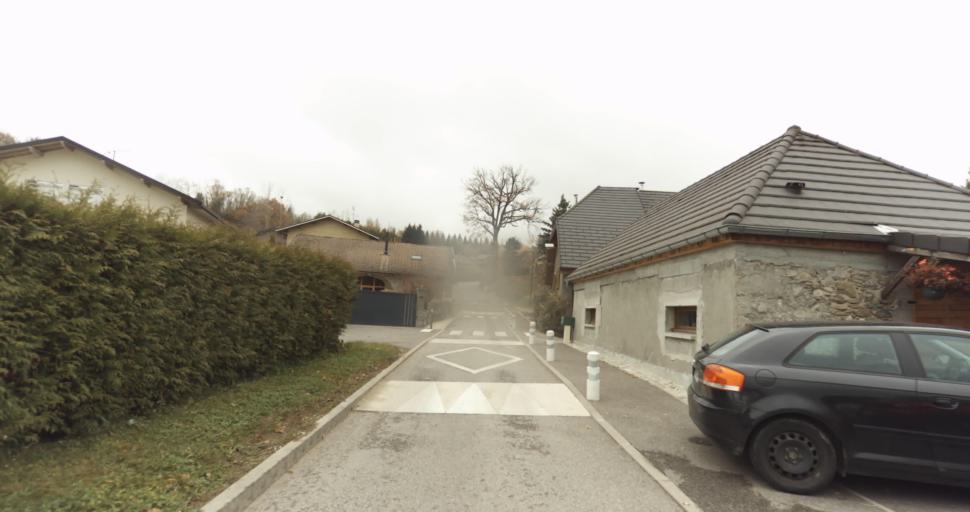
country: FR
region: Rhone-Alpes
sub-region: Departement de la Haute-Savoie
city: Groisy
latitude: 46.0011
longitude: 6.1799
